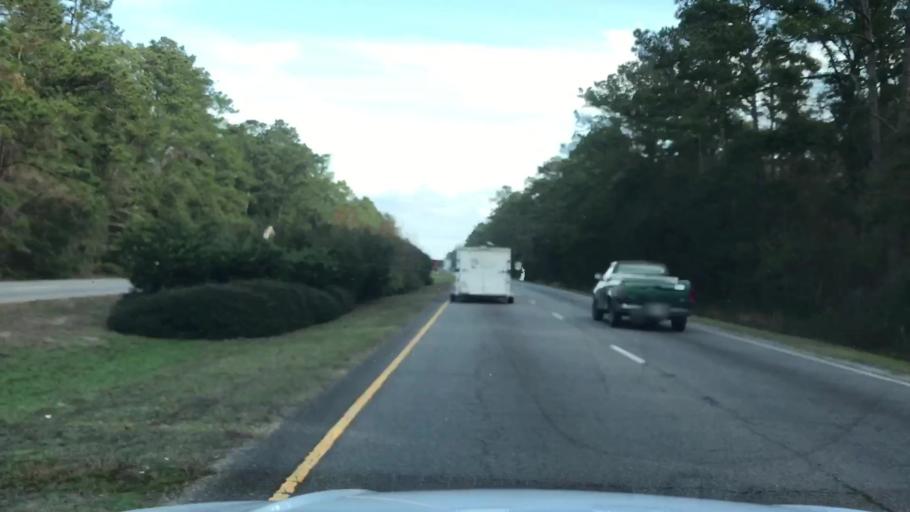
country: US
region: South Carolina
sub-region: Georgetown County
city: Murrells Inlet
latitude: 33.4983
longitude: -79.0845
